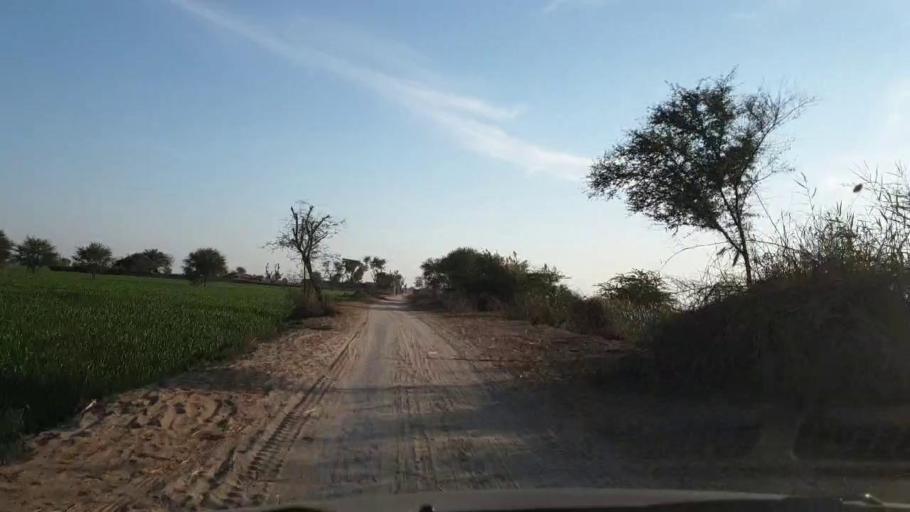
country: PK
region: Sindh
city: Khadro
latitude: 26.2230
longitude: 68.7399
